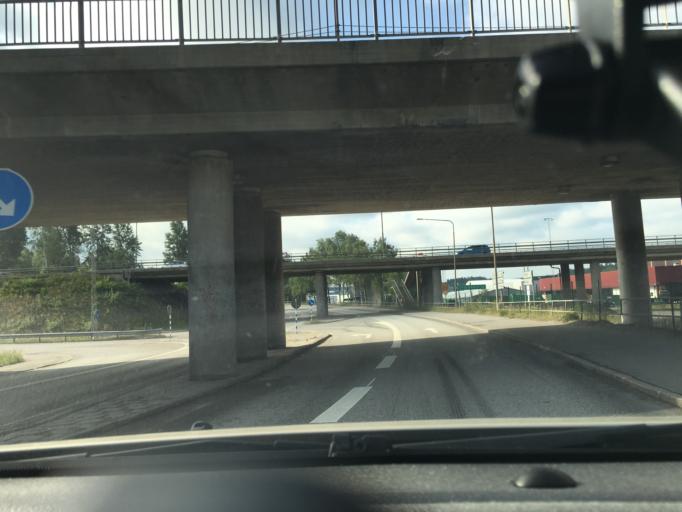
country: SE
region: Stockholm
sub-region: Sodertalje Kommun
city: Soedertaelje
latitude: 59.1774
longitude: 17.6393
